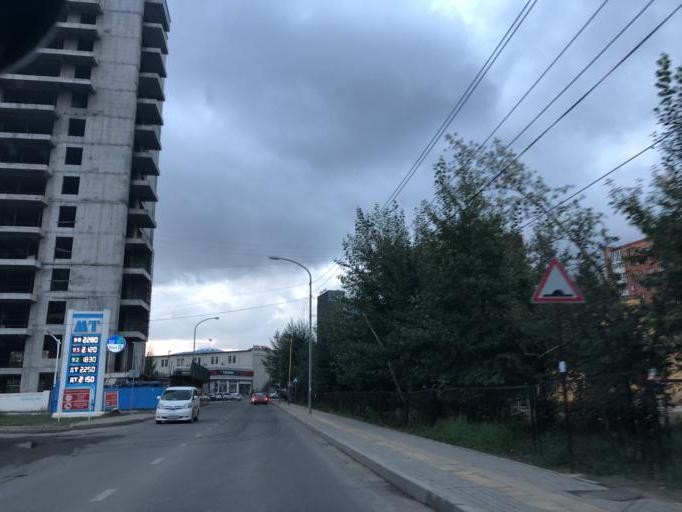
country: MN
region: Ulaanbaatar
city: Ulaanbaatar
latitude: 47.9094
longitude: 106.9074
